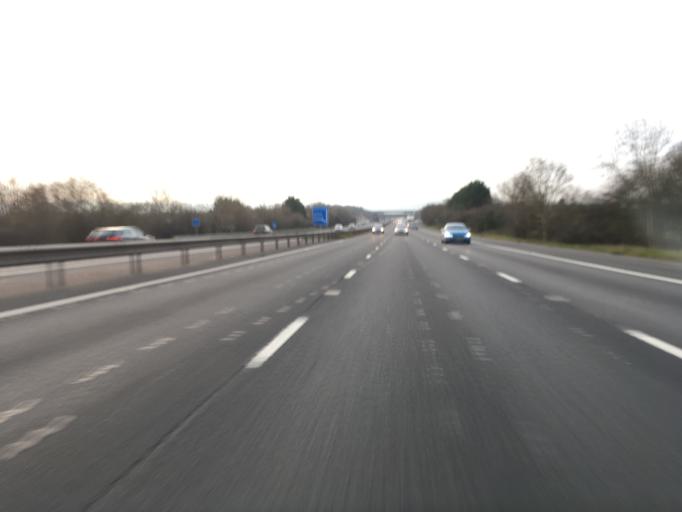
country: GB
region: England
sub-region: Gloucestershire
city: Churchdown
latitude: 51.8974
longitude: -2.1516
